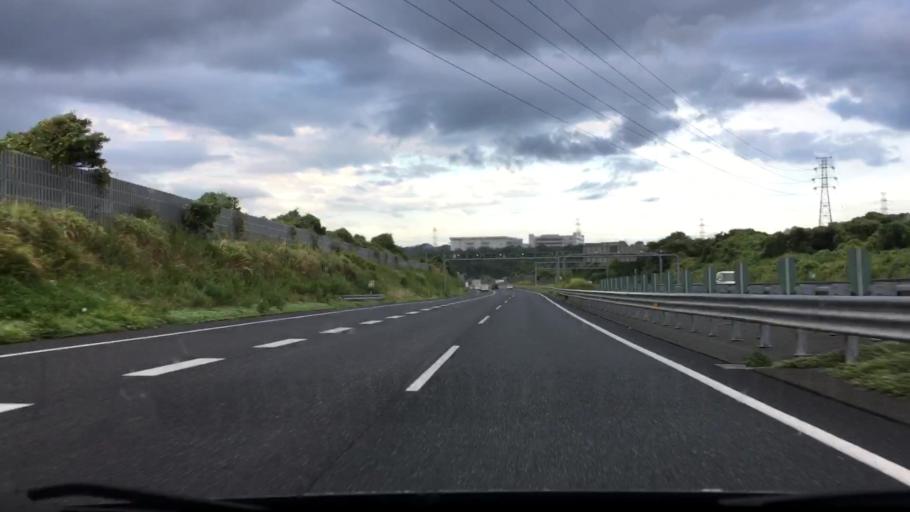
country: JP
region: Fukuoka
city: Kitakyushu
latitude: 33.8243
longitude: 130.8921
